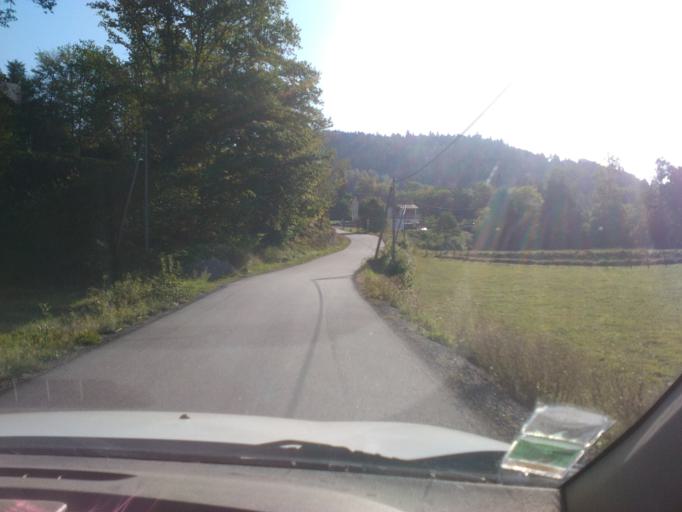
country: FR
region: Lorraine
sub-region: Departement des Vosges
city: Vagney
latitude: 48.0227
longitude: 6.7160
